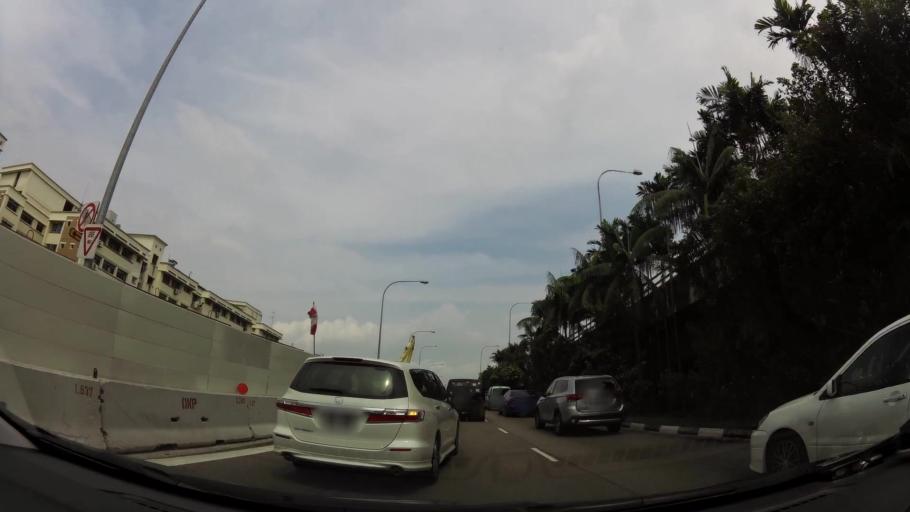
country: SG
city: Singapore
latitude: 1.3532
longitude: 103.9638
